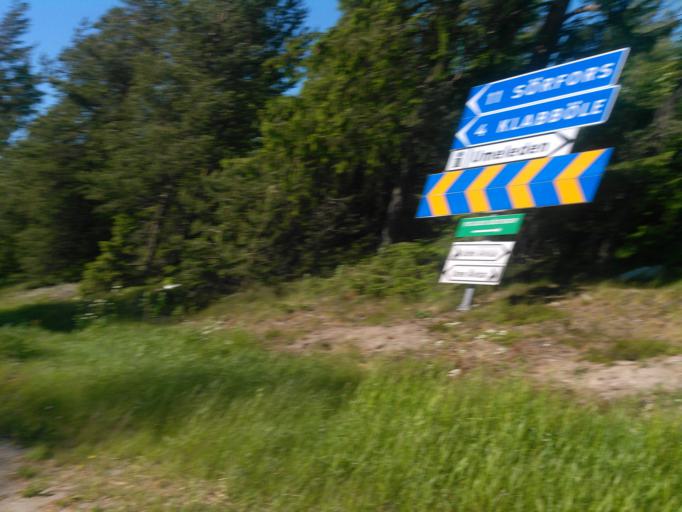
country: SE
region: Vaesterbotten
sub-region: Umea Kommun
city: Roback
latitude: 63.8245
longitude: 20.1774
